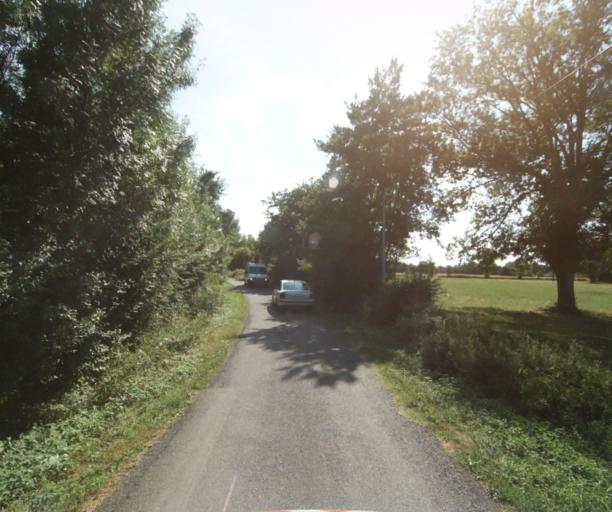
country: FR
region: Midi-Pyrenees
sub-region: Departement de la Haute-Garonne
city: Revel
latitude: 43.4799
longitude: 1.9919
